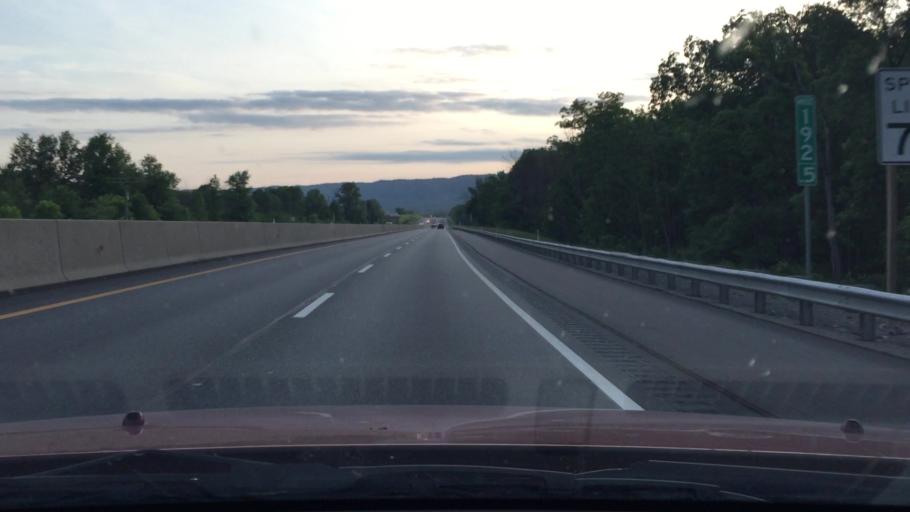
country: US
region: Pennsylvania
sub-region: Franklin County
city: Doylestown
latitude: 40.1265
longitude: -77.7509
